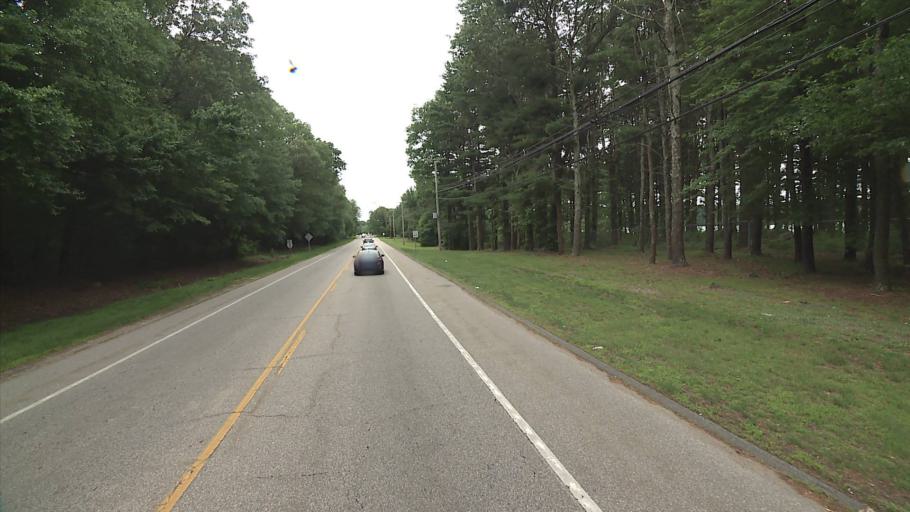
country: US
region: Connecticut
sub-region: New London County
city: Poquonock Bridge
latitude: 41.3581
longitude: -72.0283
